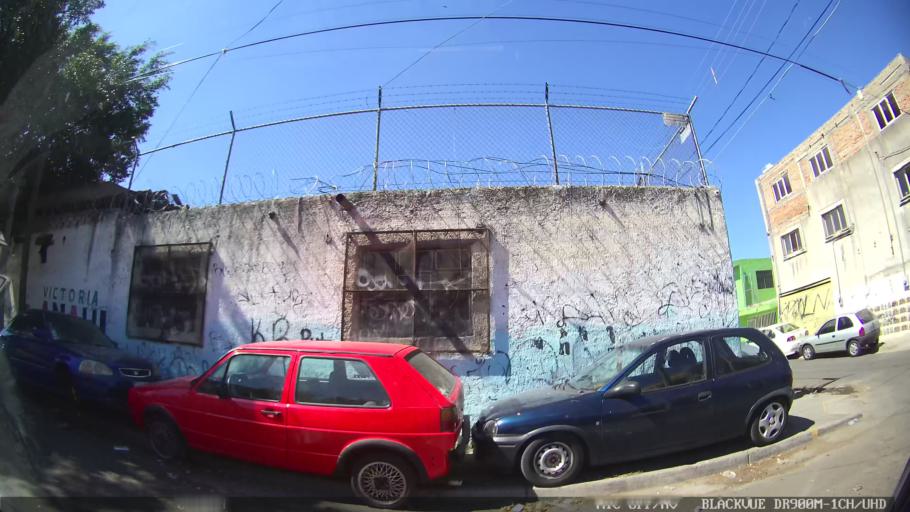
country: MX
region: Jalisco
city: Tlaquepaque
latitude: 20.6978
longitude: -103.2802
